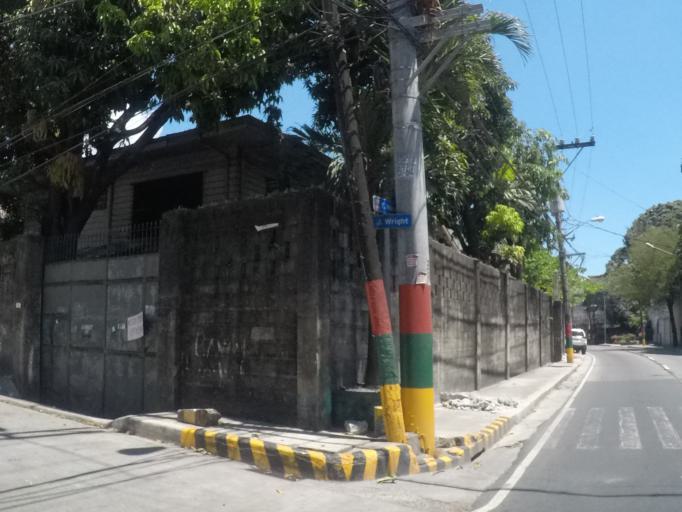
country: PH
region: Metro Manila
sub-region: San Juan
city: San Juan
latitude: 14.5991
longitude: 121.0248
